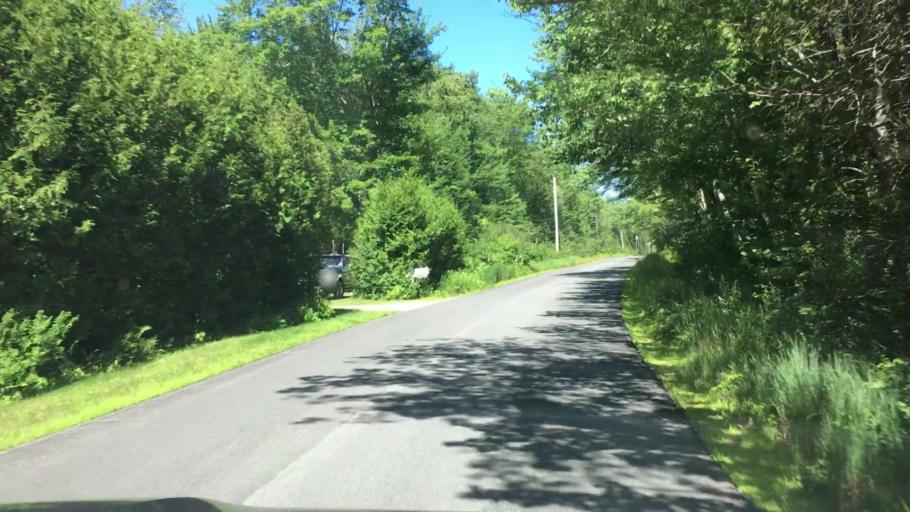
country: US
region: Maine
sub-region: Hancock County
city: Sedgwick
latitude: 44.3160
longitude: -68.6193
